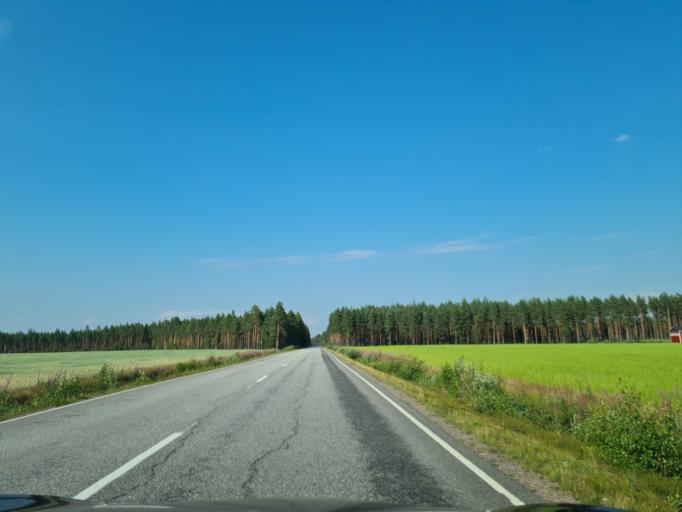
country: FI
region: Satakunta
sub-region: Pohjois-Satakunta
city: Karvia
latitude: 62.2970
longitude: 22.6268
